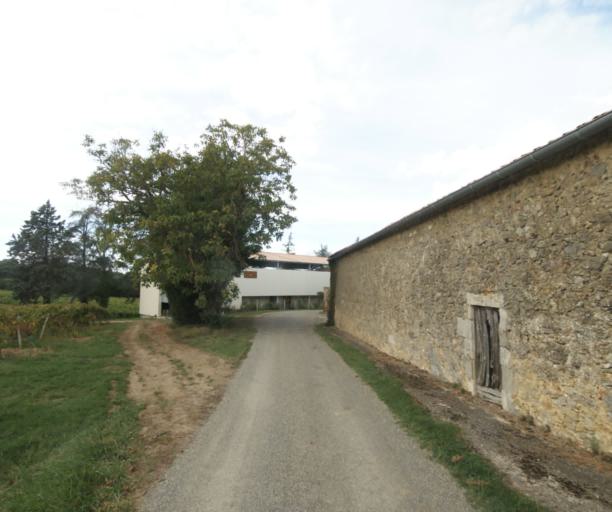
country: FR
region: Midi-Pyrenees
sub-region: Departement du Gers
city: Gondrin
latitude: 43.8676
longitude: 0.2673
